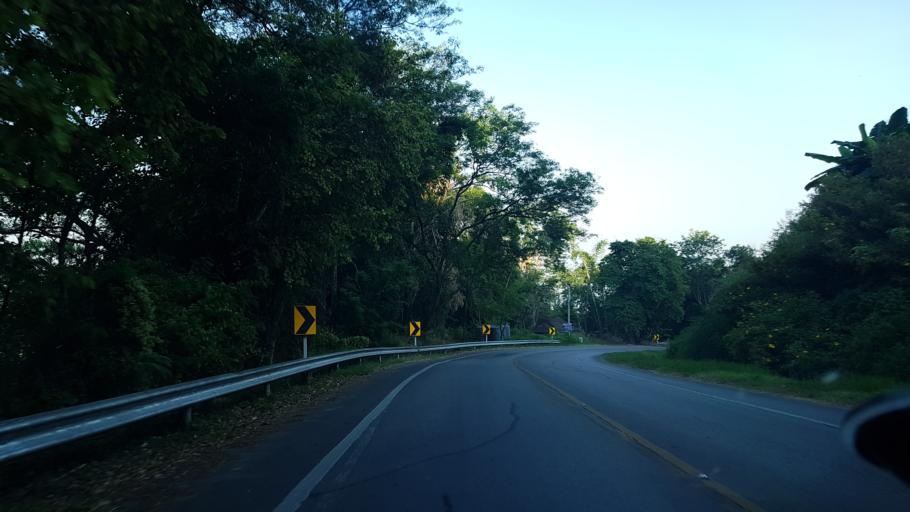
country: TH
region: Chiang Rai
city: Mae Fa Luang
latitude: 20.2947
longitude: 99.8158
